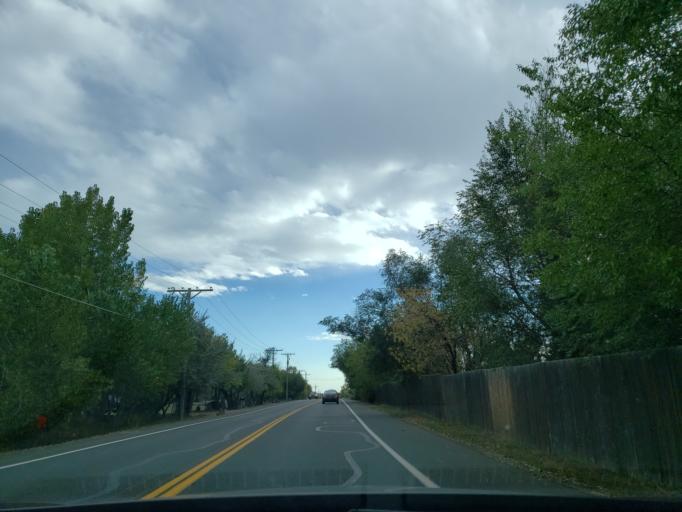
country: US
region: Colorado
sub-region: Larimer County
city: Fort Collins
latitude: 40.6153
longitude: -105.0387
